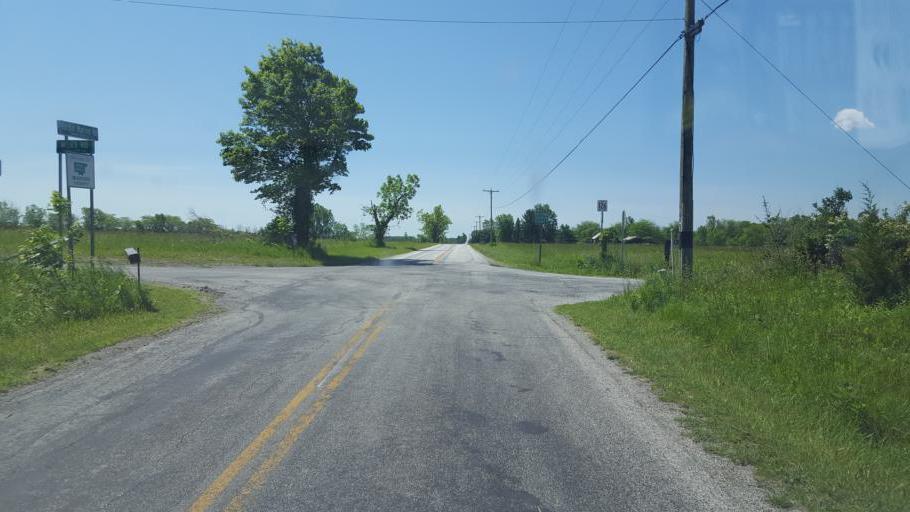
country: US
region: Ohio
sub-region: Hardin County
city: Forest
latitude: 40.6510
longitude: -83.4197
